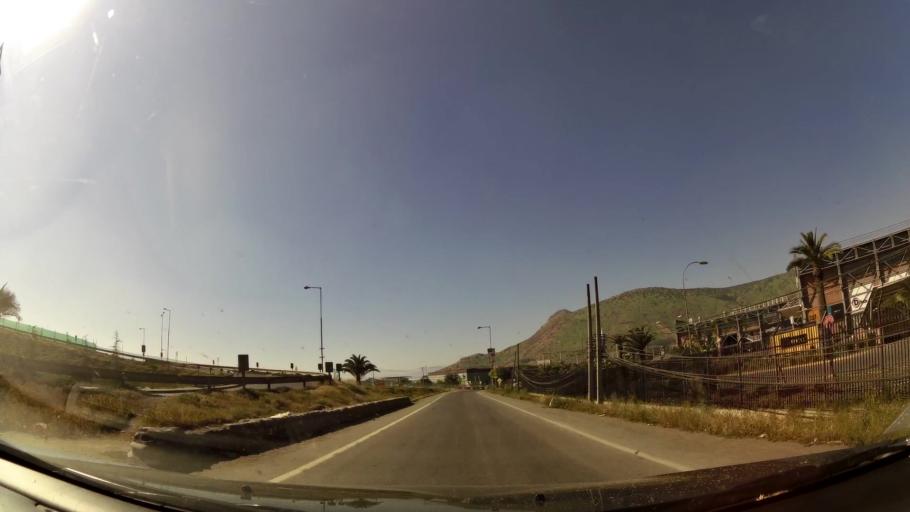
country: CL
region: Santiago Metropolitan
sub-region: Provincia de Chacabuco
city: Chicureo Abajo
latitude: -33.3346
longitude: -70.7137
